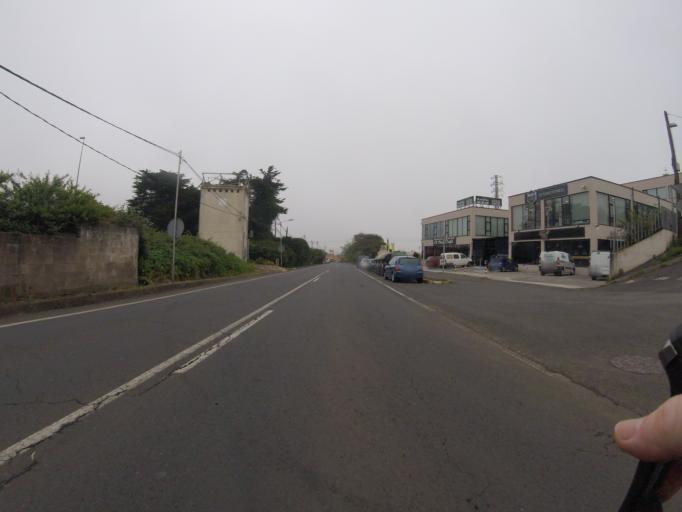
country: ES
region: Canary Islands
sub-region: Provincia de Santa Cruz de Tenerife
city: La Laguna
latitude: 28.4916
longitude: -16.3642
